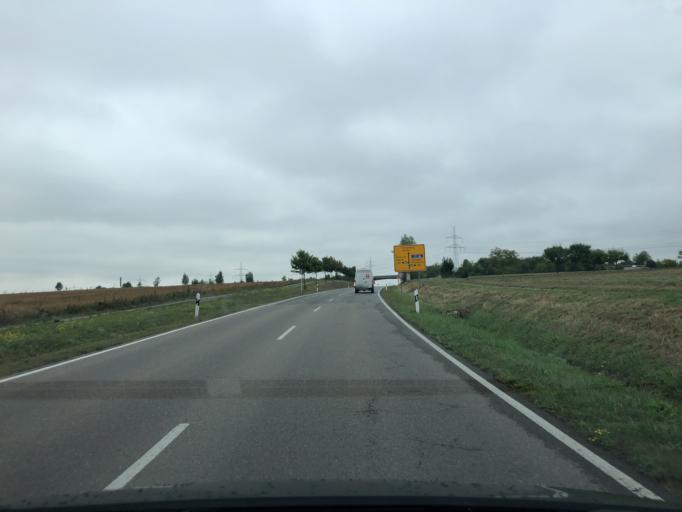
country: DE
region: Baden-Wuerttemberg
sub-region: Regierungsbezirk Stuttgart
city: Bondorf
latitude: 48.5040
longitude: 8.8176
